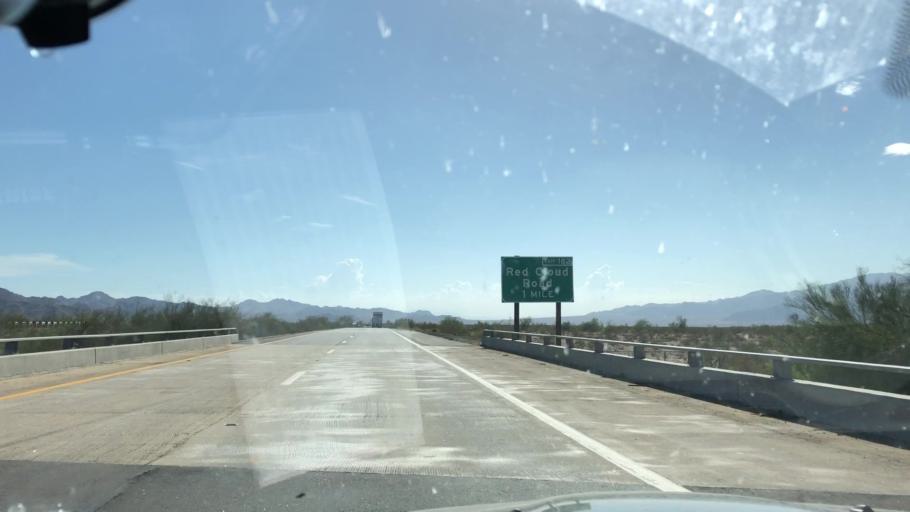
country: US
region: California
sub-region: Imperial County
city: Niland
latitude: 33.6821
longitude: -115.5446
